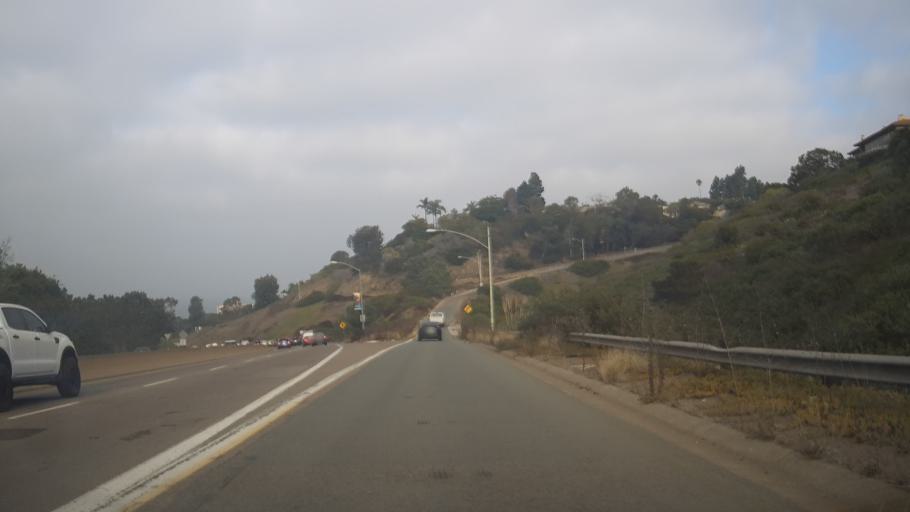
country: US
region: California
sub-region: San Diego County
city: La Jolla
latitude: 32.8452
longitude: -117.2421
